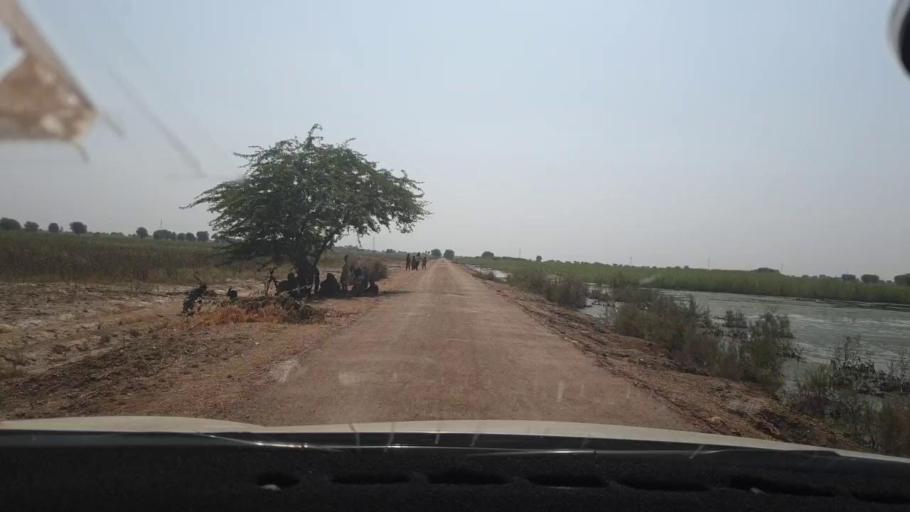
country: PK
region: Sindh
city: Tando Mittha Khan
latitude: 25.9137
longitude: 69.2067
